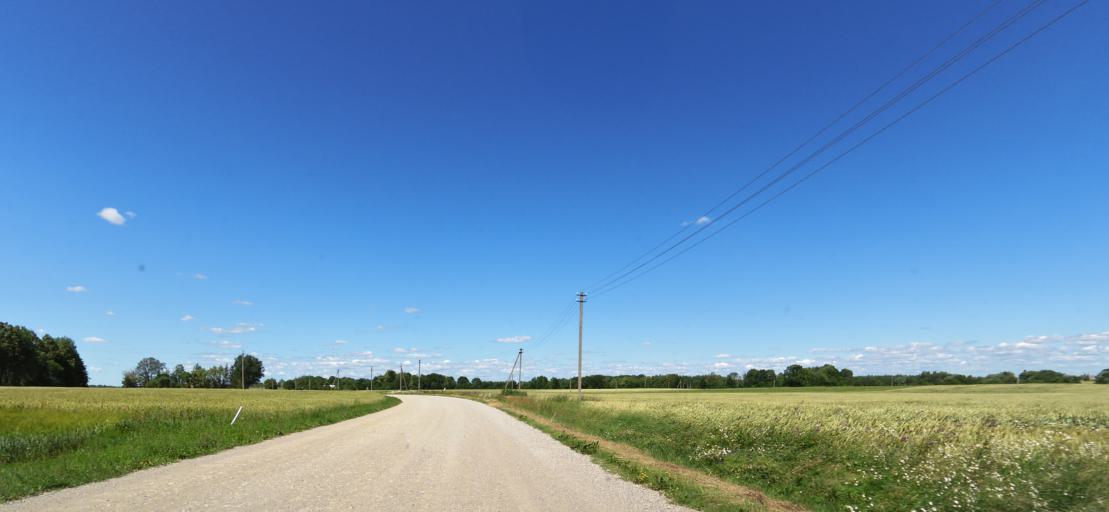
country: LT
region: Panevezys
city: Pasvalys
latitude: 56.2562
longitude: 24.3603
